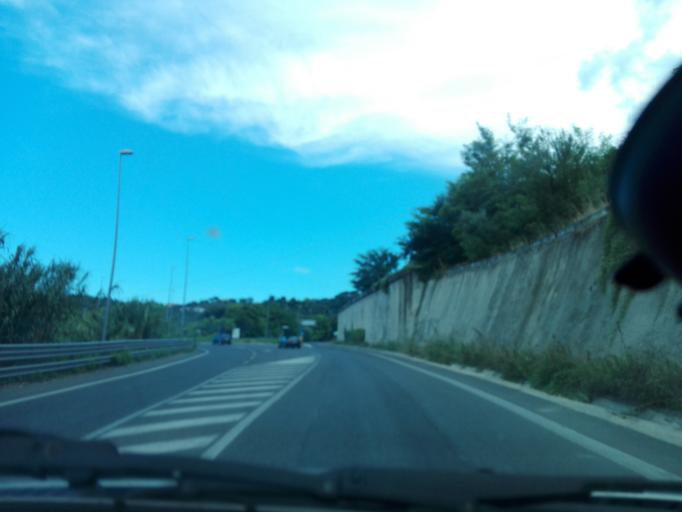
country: IT
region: Abruzzo
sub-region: Provincia di Pescara
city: Montesilvano Marina
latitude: 42.4991
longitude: 14.1415
